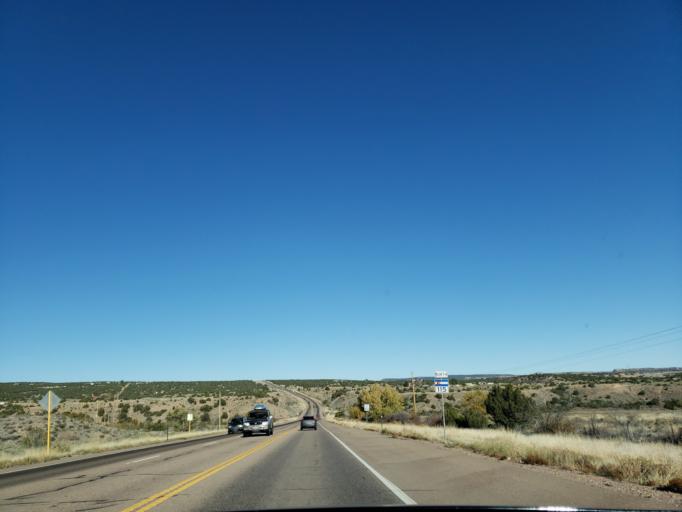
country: US
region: Colorado
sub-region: Fremont County
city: Penrose
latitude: 38.4667
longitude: -104.9959
